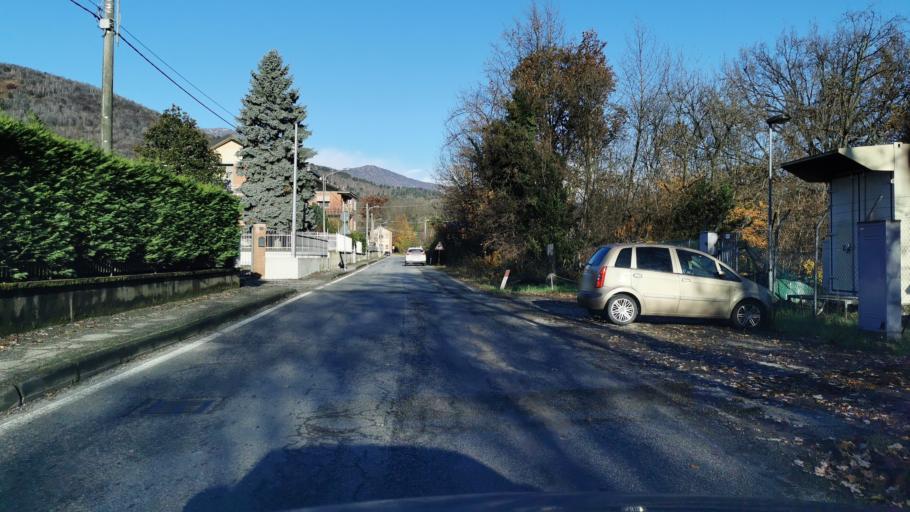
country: IT
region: Piedmont
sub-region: Provincia di Torino
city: La Cassa
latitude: 45.1765
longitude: 7.5179
